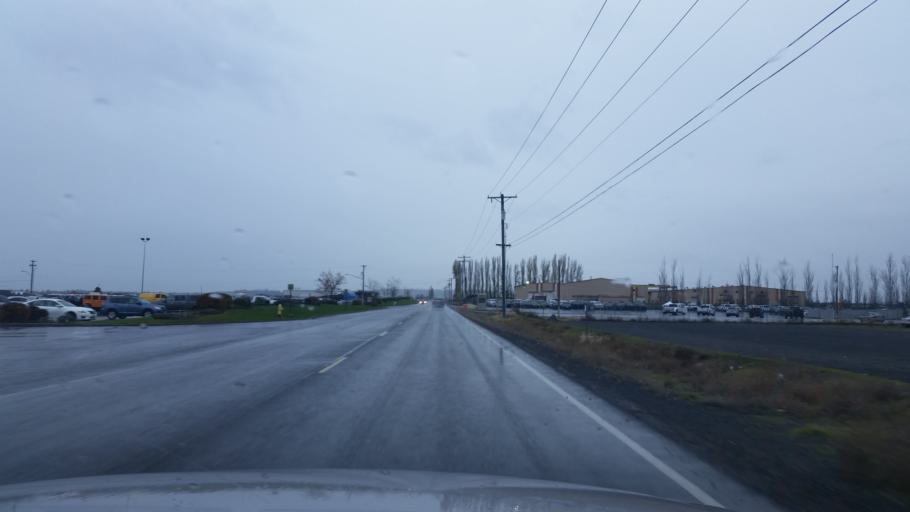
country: US
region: Washington
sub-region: Spokane County
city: Airway Heights
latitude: 47.6346
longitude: -117.5610
